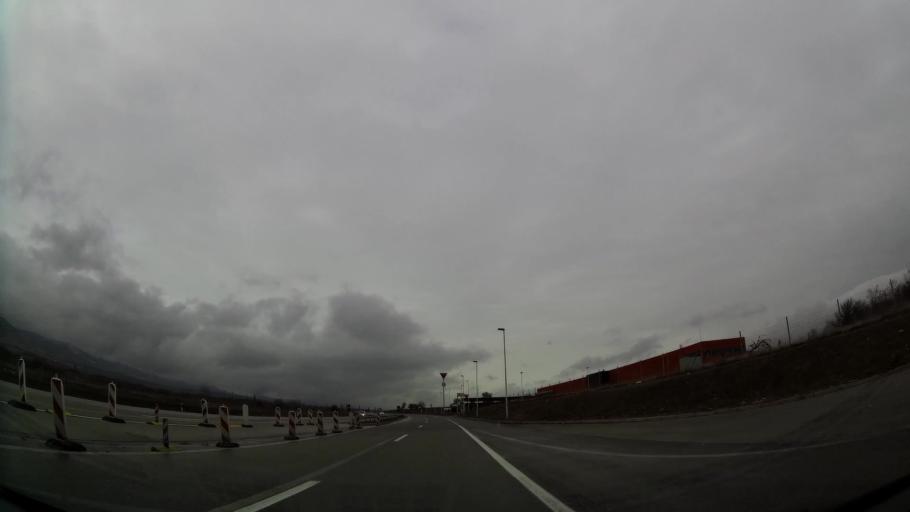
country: MK
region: Opstina Lipkovo
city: Lojane
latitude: 42.2431
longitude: 21.7024
